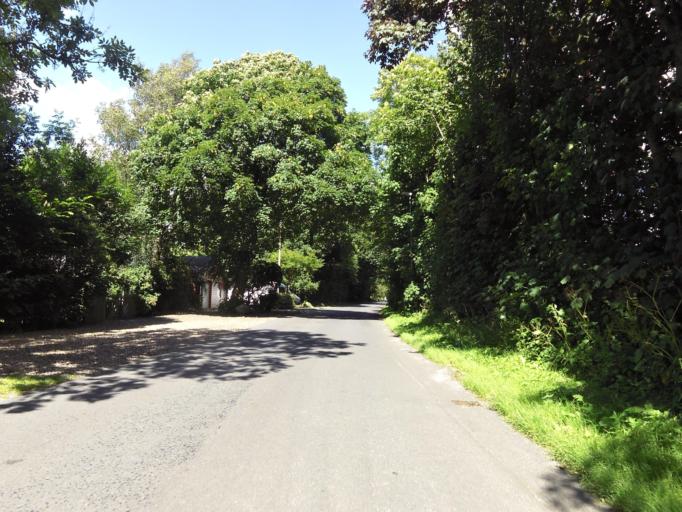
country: DK
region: South Denmark
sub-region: Haderslev Kommune
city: Gram
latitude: 55.3093
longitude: 9.1517
